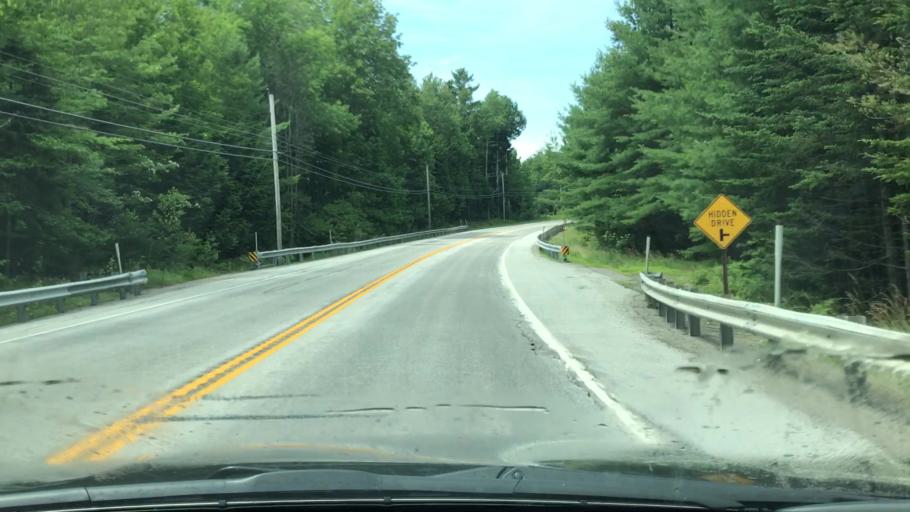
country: US
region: Maine
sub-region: Waldo County
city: Northport
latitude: 44.3421
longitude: -68.9680
